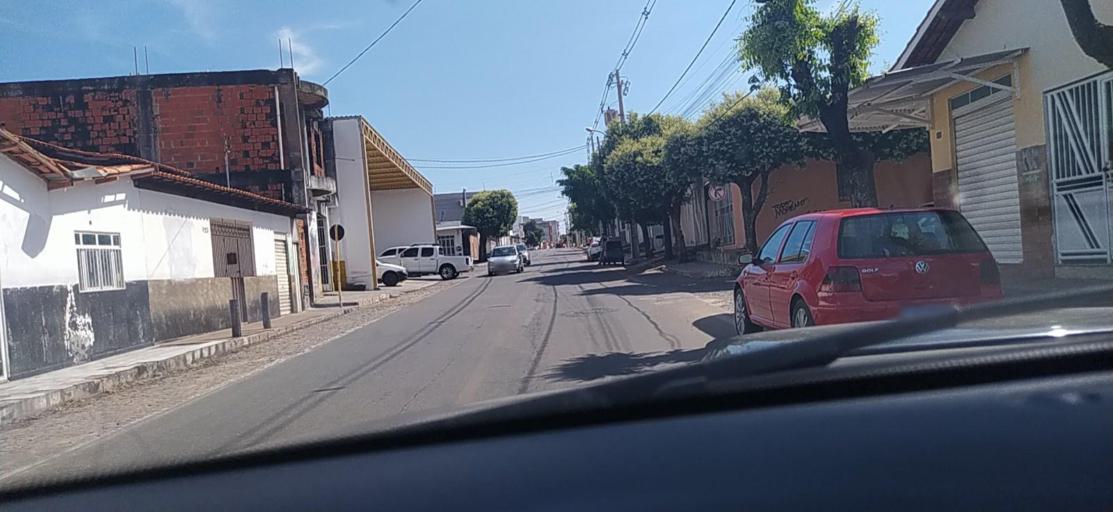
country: BR
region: Bahia
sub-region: Guanambi
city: Guanambi
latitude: -14.2188
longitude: -42.7728
